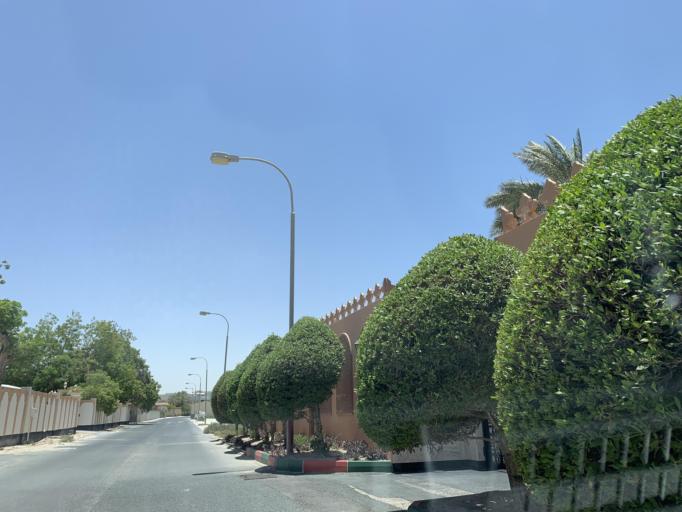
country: BH
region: Manama
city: Jidd Hafs
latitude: 26.2244
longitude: 50.4846
